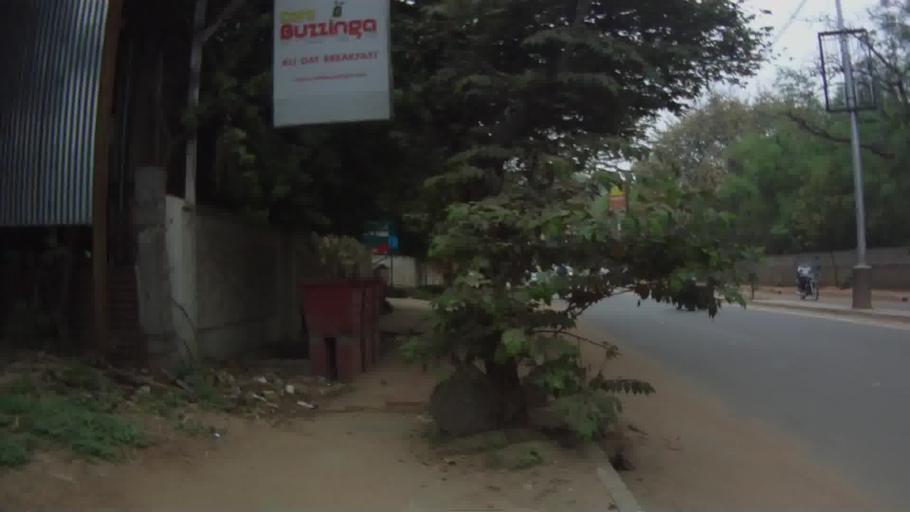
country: IN
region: Karnataka
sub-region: Bangalore Rural
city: Hoskote
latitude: 12.9564
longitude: 77.7327
